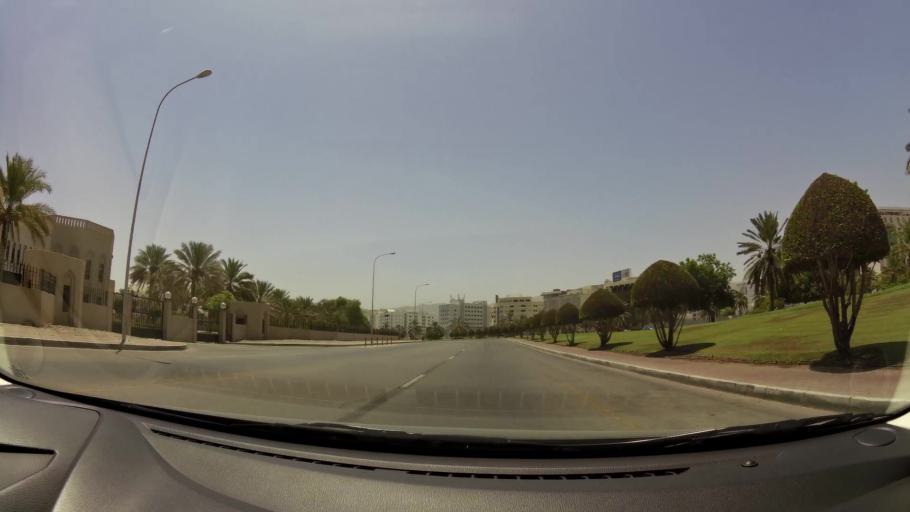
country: OM
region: Muhafazat Masqat
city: Bawshar
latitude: 23.5982
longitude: 58.4251
